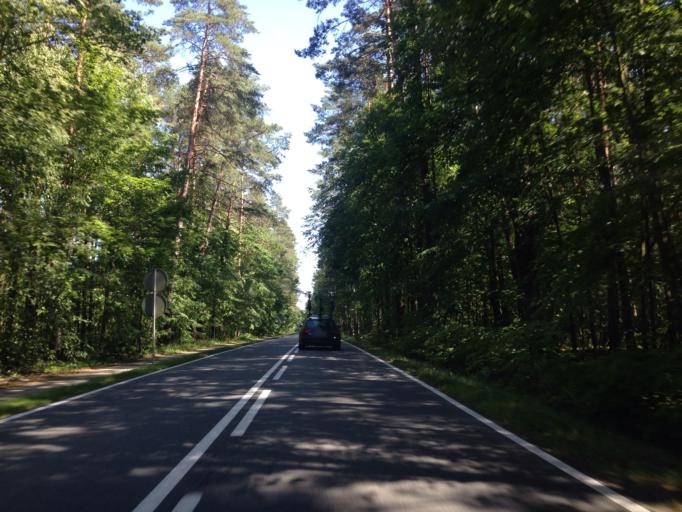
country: PL
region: Kujawsko-Pomorskie
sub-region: Powiat swiecki
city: Osie
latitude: 53.6137
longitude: 18.2868
